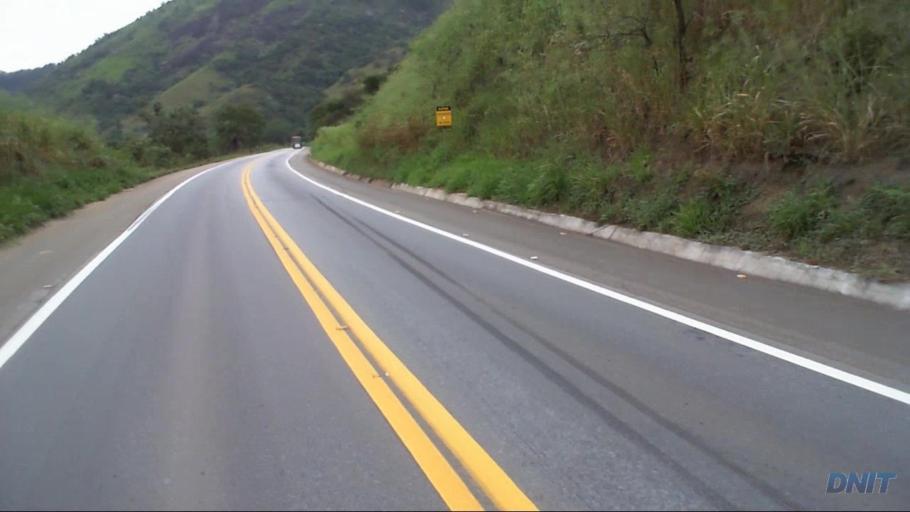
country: BR
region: Minas Gerais
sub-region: Timoteo
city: Timoteo
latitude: -19.5748
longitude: -42.7186
